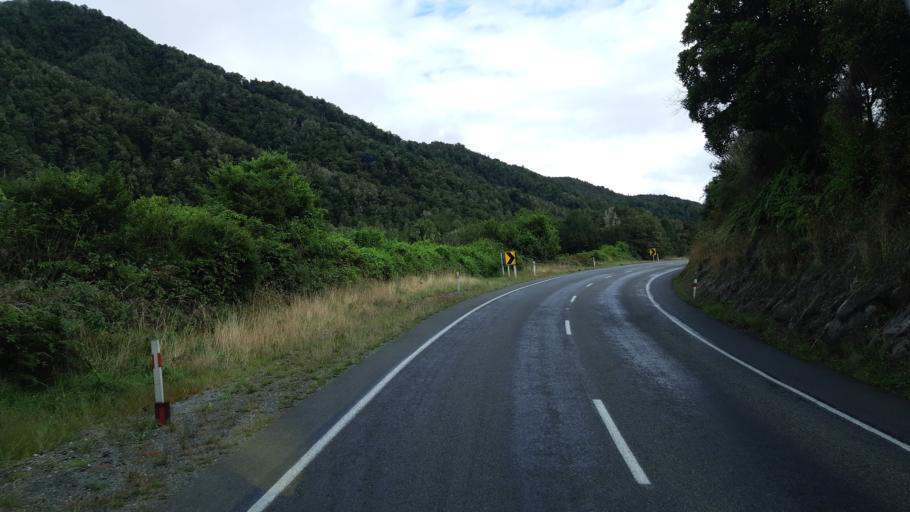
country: NZ
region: West Coast
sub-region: Buller District
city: Westport
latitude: -41.8397
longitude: 172.2434
